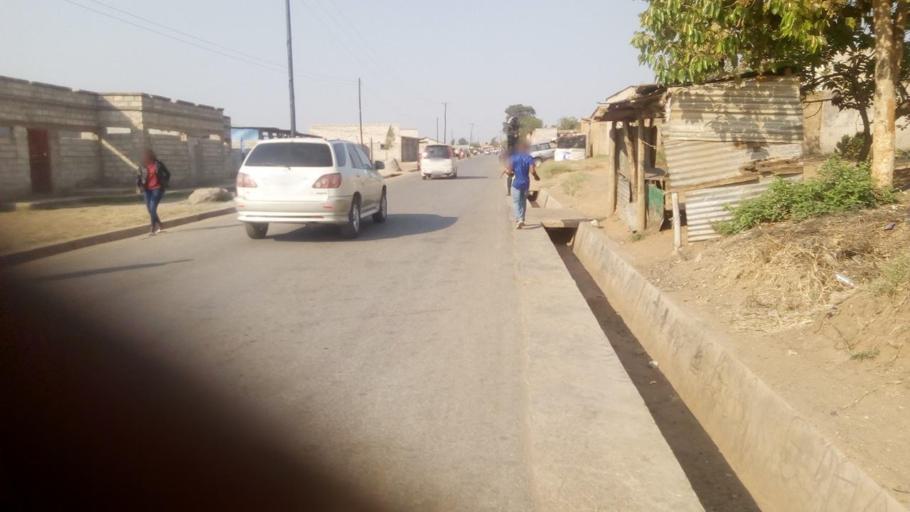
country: ZM
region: Lusaka
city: Lusaka
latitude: -15.3684
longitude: 28.2969
